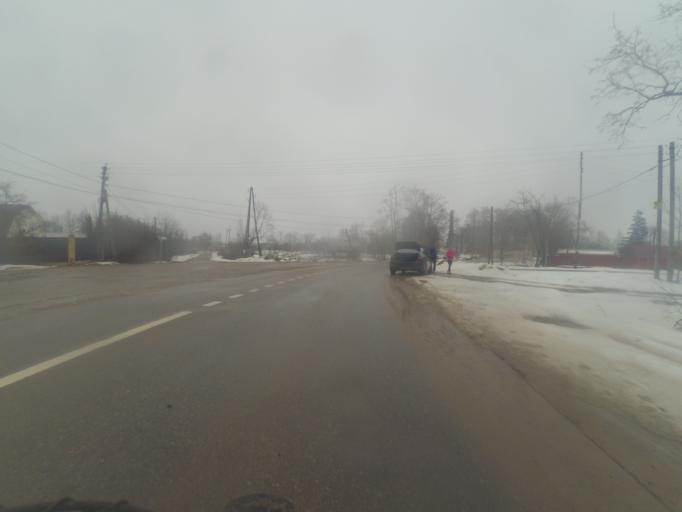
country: RU
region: Moskovskaya
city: Avtopoligon
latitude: 56.2600
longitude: 37.2502
